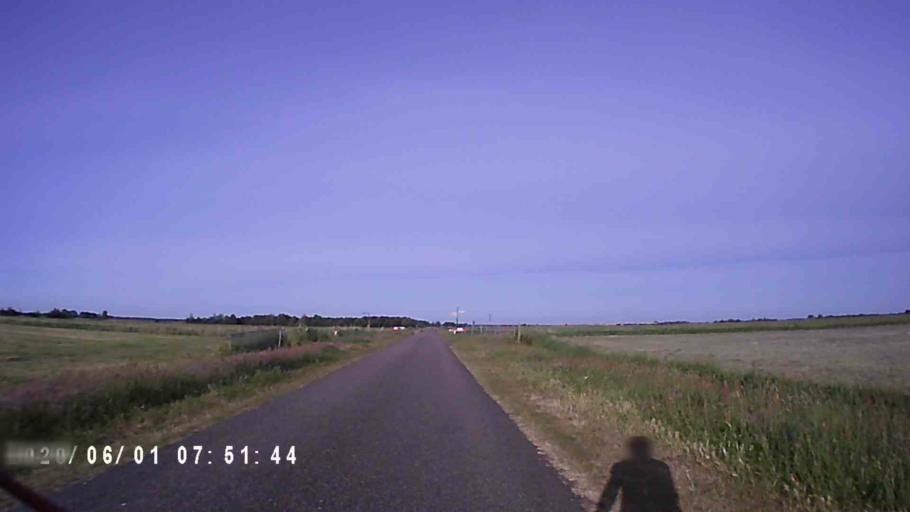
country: NL
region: Friesland
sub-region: Gemeente Dantumadiel
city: Rinsumageast
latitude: 53.2858
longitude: 5.9431
